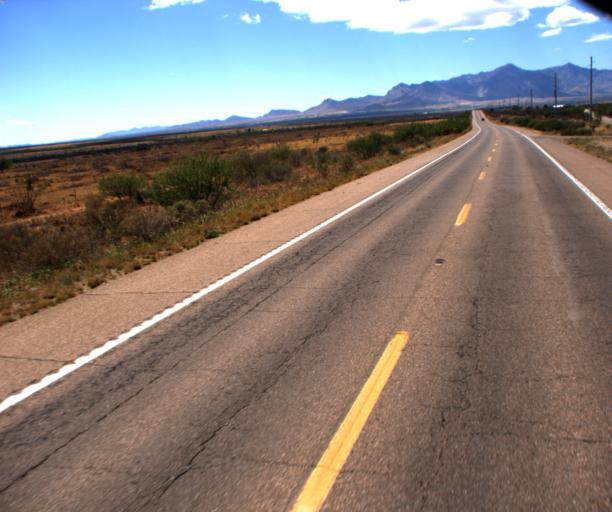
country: US
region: Arizona
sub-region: Cochise County
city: Naco
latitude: 31.3799
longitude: -110.0386
